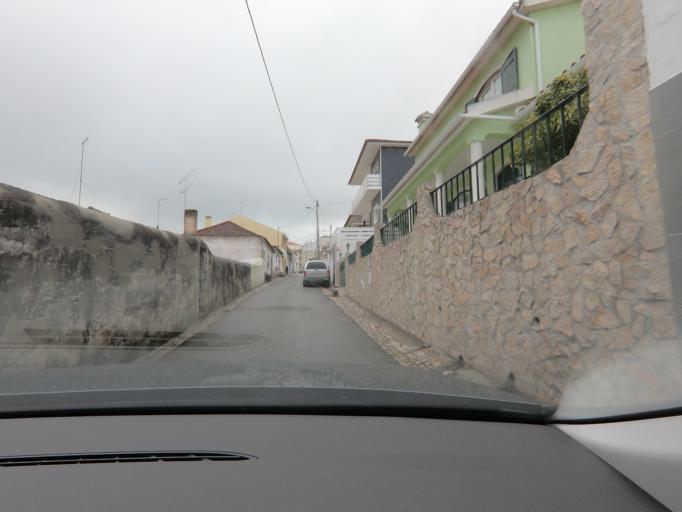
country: PT
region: Lisbon
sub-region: Alenquer
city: Alenquer
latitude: 39.0494
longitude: -9.0023
